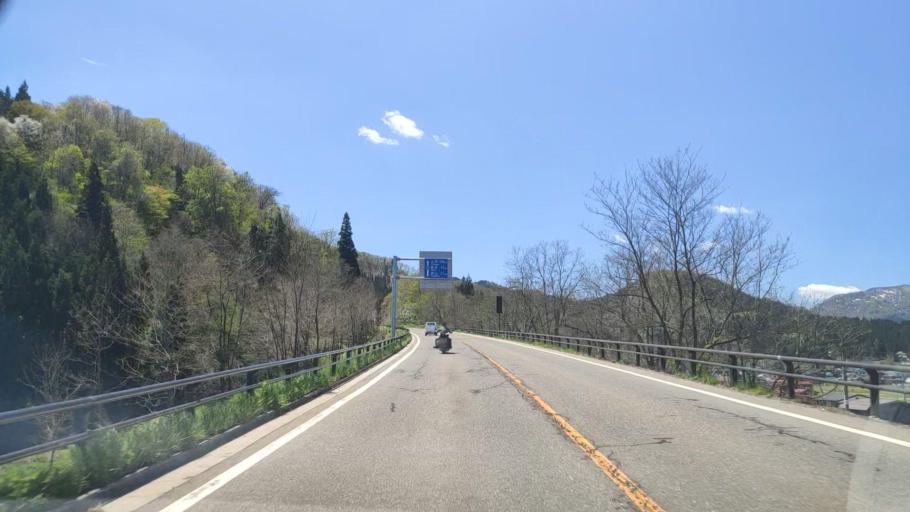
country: JP
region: Akita
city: Yuzawa
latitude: 39.0511
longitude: 140.4269
